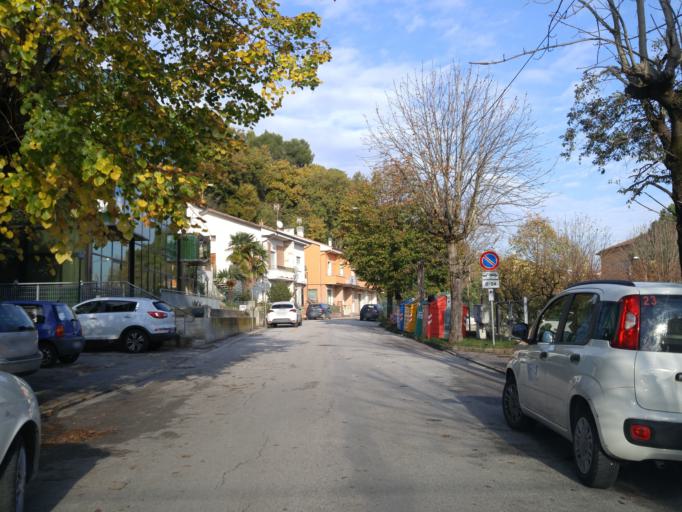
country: IT
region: The Marches
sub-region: Provincia di Pesaro e Urbino
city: Calcinelli
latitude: 43.7518
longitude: 12.9166
